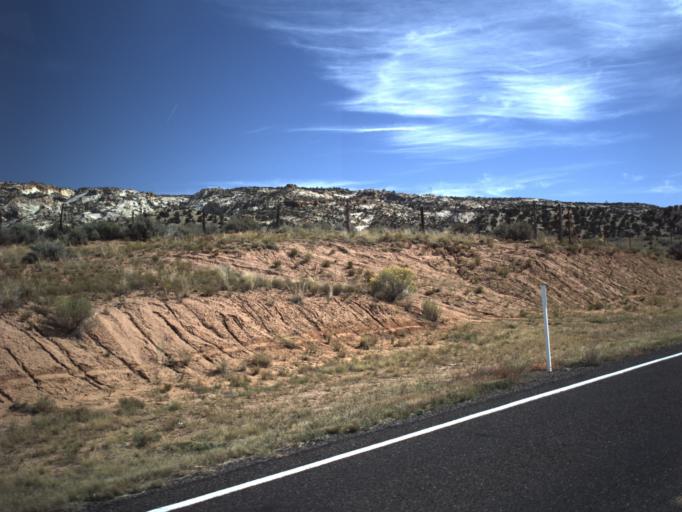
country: US
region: Utah
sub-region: Wayne County
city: Loa
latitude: 37.7637
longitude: -111.5830
